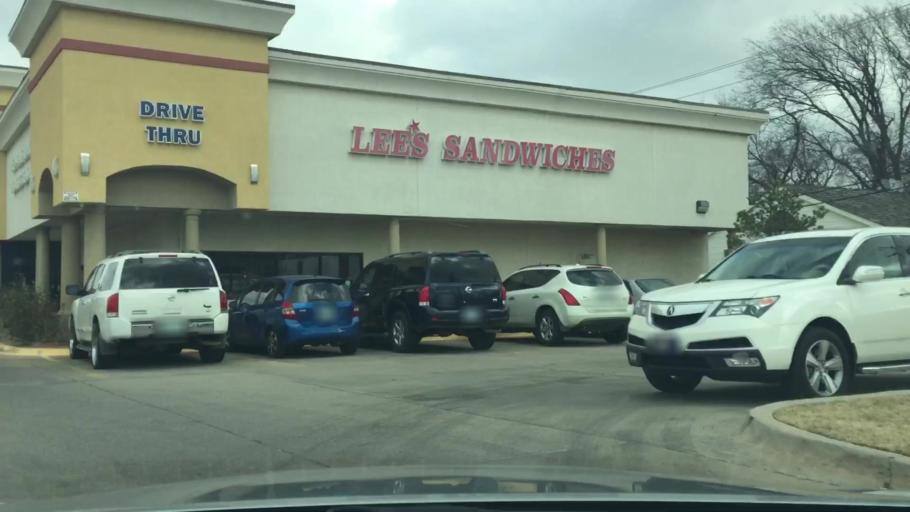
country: US
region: Oklahoma
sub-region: Oklahoma County
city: Oklahoma City
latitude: 35.5030
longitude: -97.5338
